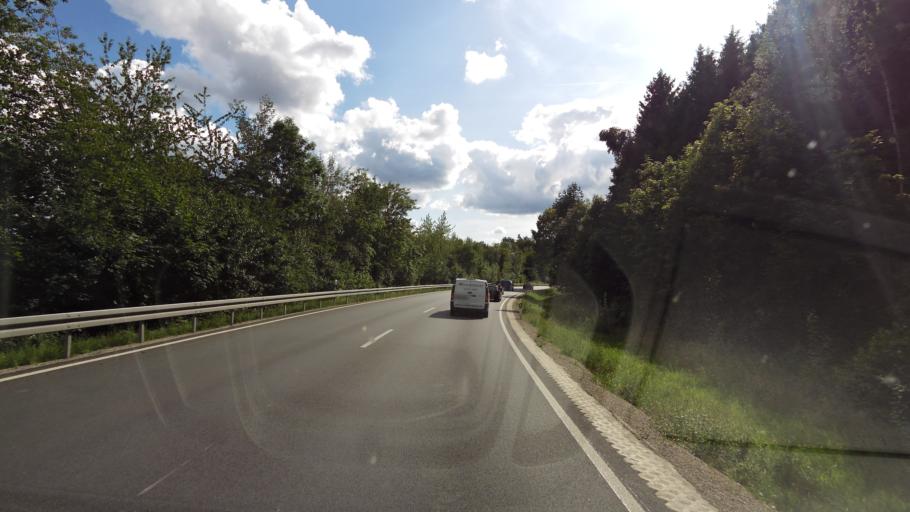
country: DE
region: Bavaria
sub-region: Lower Bavaria
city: Loitzendorf
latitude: 49.0921
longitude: 12.6464
